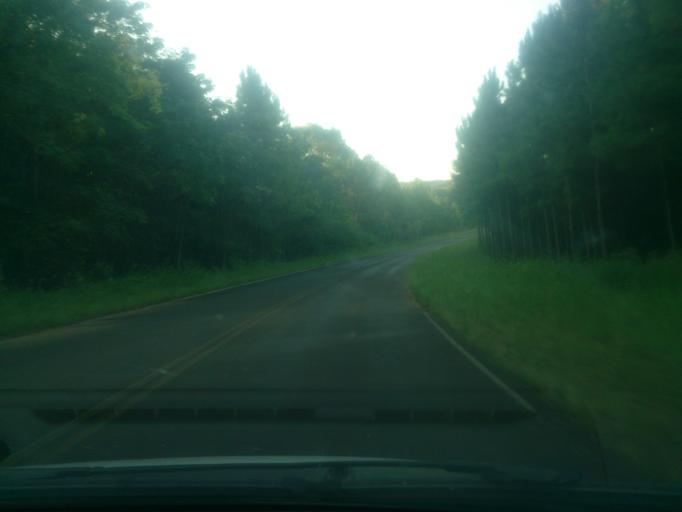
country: AR
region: Misiones
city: Panambi
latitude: -27.6729
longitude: -54.9120
